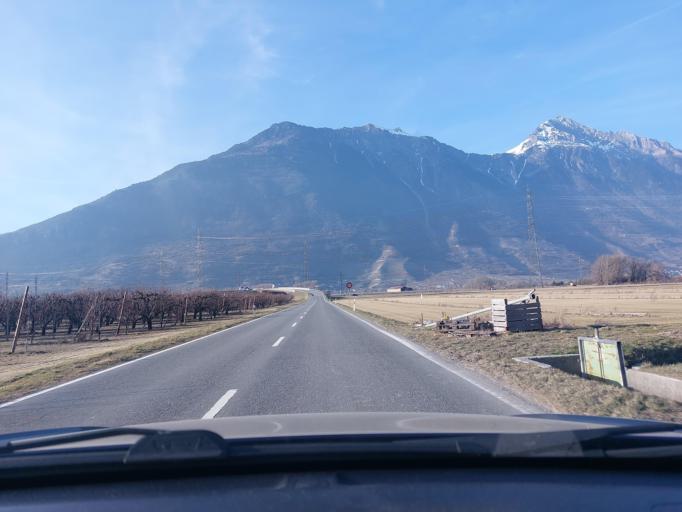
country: CH
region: Valais
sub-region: Martigny District
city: Fully
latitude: 46.1106
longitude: 7.1021
